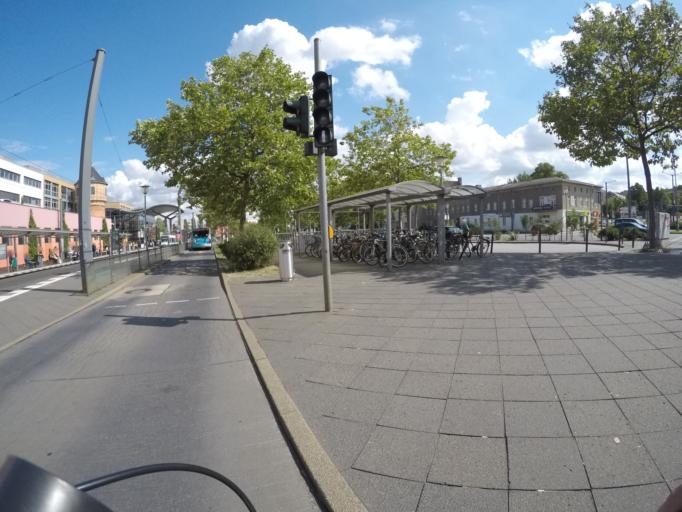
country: DE
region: Brandenburg
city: Potsdam
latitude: 52.3909
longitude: 13.0650
